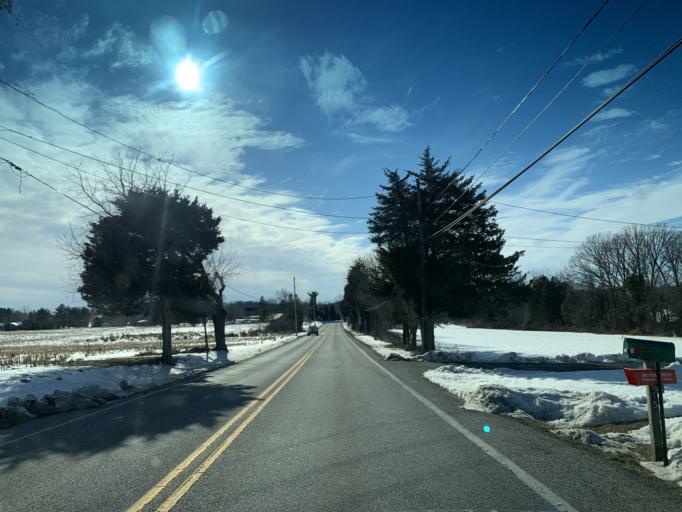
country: US
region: Pennsylvania
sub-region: York County
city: Dillsburg
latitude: 40.0498
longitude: -76.9577
